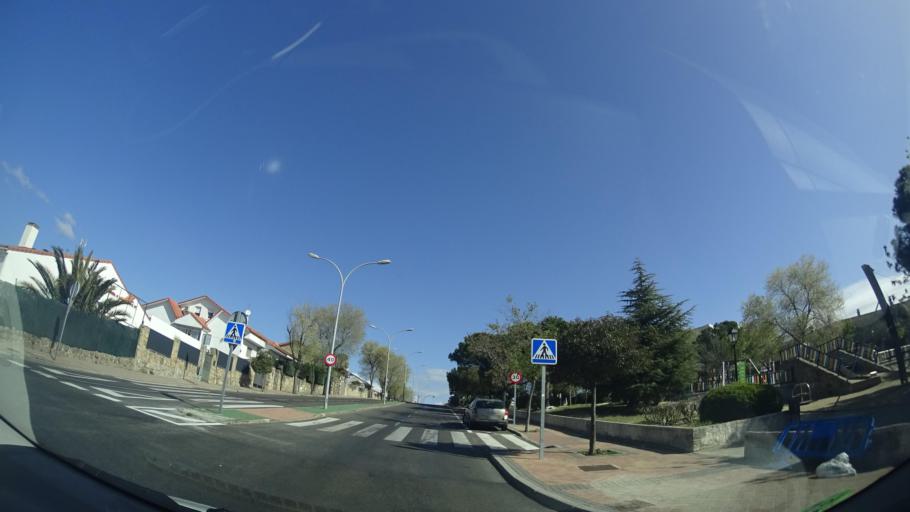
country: ES
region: Madrid
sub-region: Provincia de Madrid
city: Colmenar Viejo
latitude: 40.6589
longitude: -3.7763
